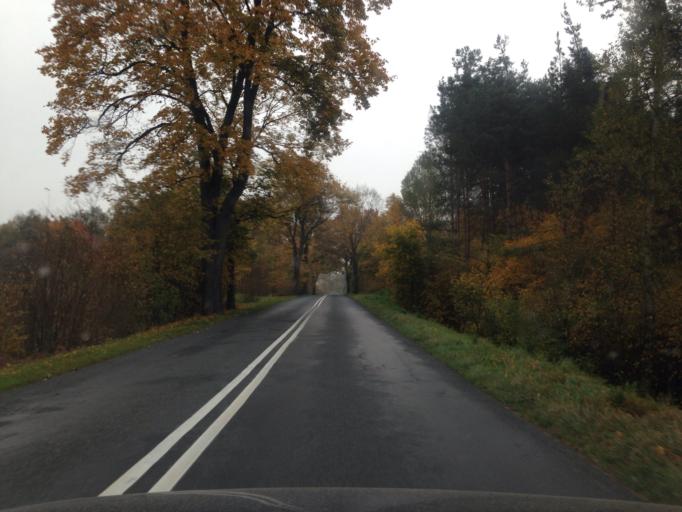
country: PL
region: Kujawsko-Pomorskie
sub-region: Powiat brodnicki
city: Bartniczka
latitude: 53.2455
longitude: 19.6431
